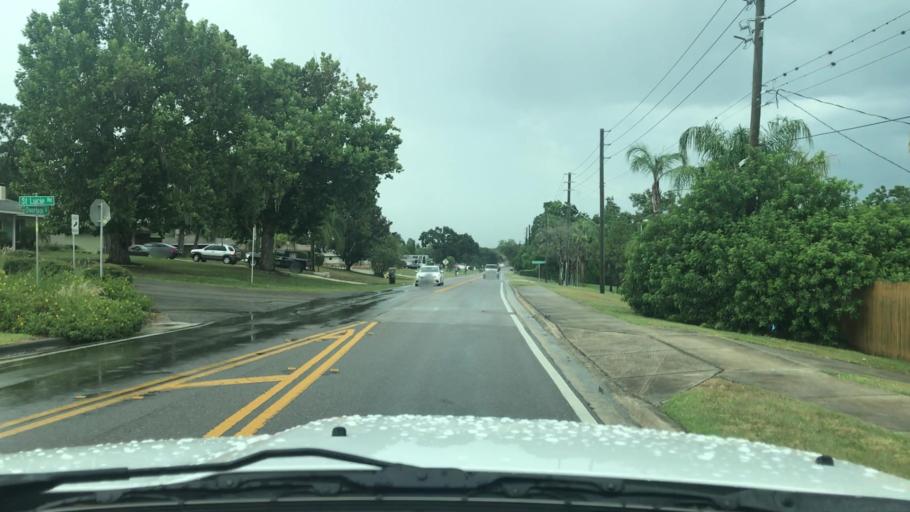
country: US
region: Florida
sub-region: Polk County
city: Cypress Gardens
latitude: 28.0044
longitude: -81.6899
